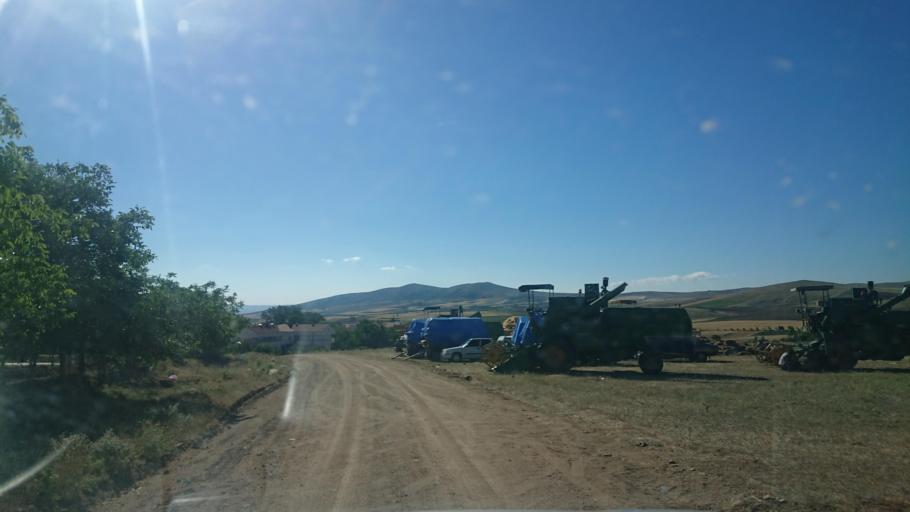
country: TR
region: Aksaray
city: Agacoren
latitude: 38.8269
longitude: 33.9559
